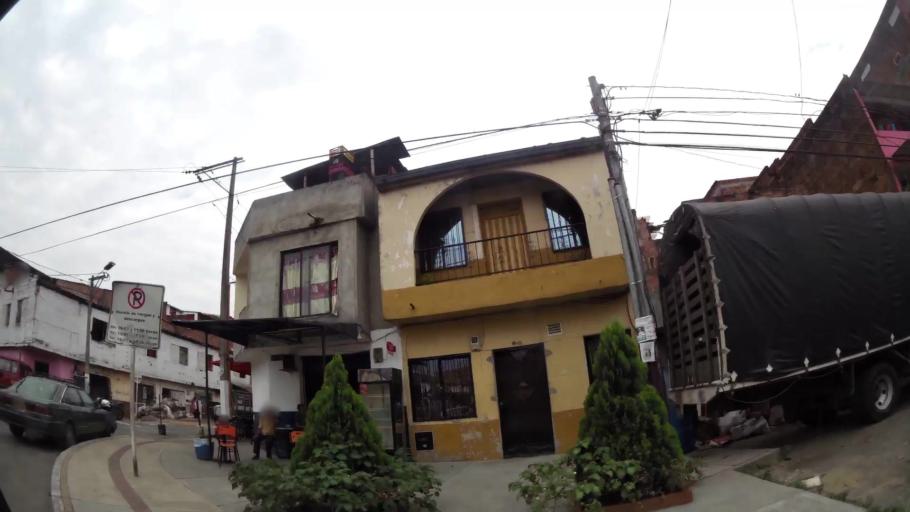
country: CO
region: Antioquia
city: Medellin
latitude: 6.2836
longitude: -75.5654
